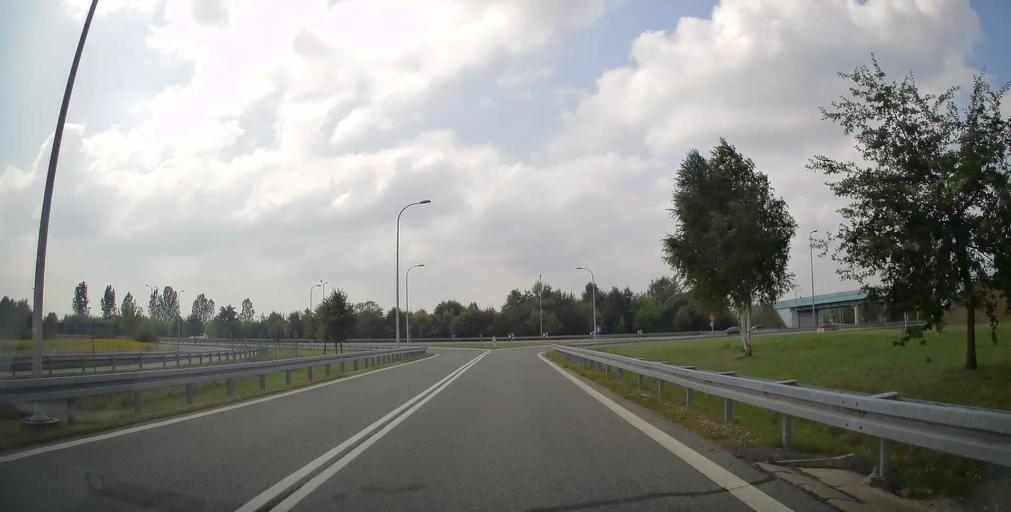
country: PL
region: Masovian Voivodeship
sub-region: Powiat bialobrzeski
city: Sucha
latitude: 51.6099
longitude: 20.9855
